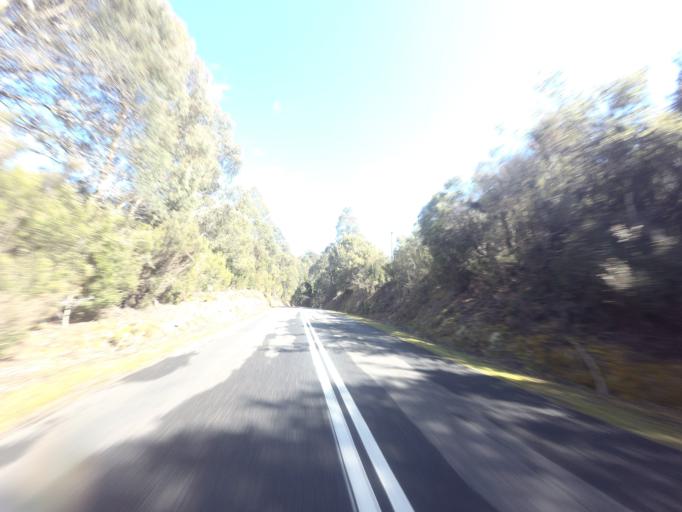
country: AU
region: Tasmania
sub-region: Derwent Valley
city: New Norfolk
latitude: -42.7545
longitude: 146.5253
